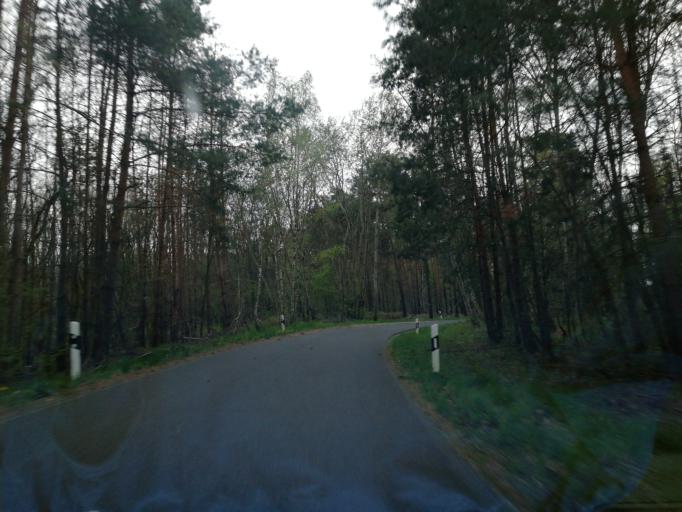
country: DE
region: Brandenburg
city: Calau
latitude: 51.7909
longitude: 13.8874
